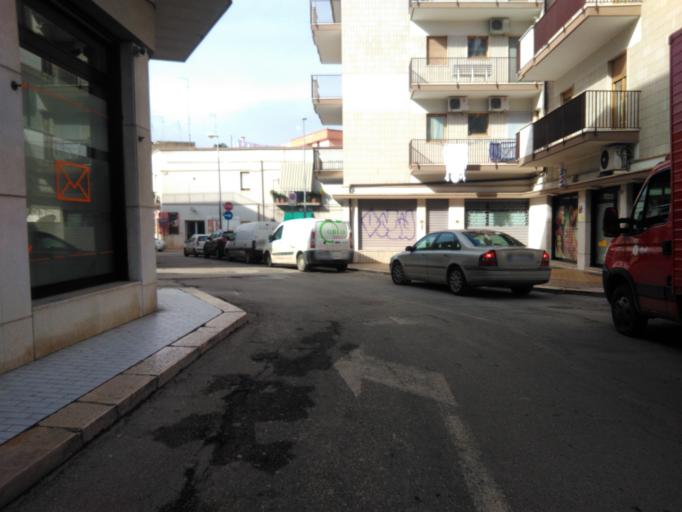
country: IT
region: Apulia
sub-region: Provincia di Barletta - Andria - Trani
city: Andria
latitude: 41.2338
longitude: 16.2971
